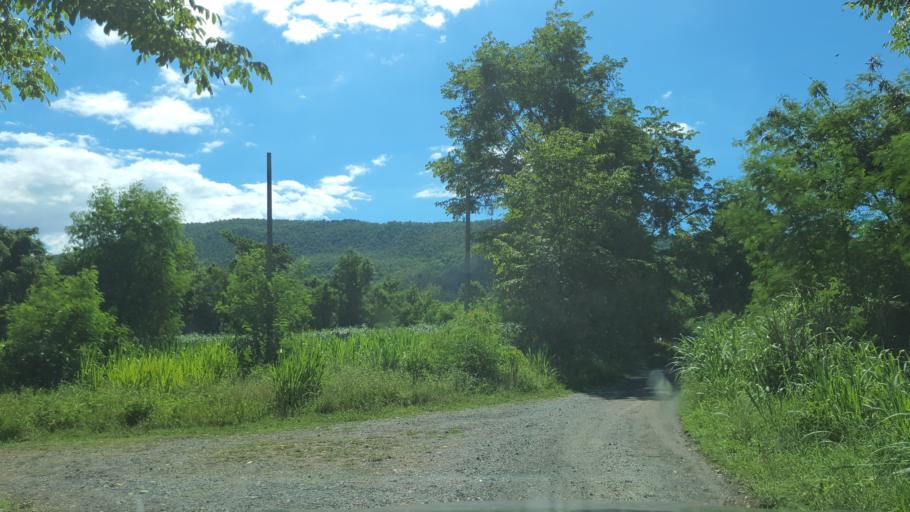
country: TH
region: Chiang Mai
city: Mae On
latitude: 18.7644
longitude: 99.2430
